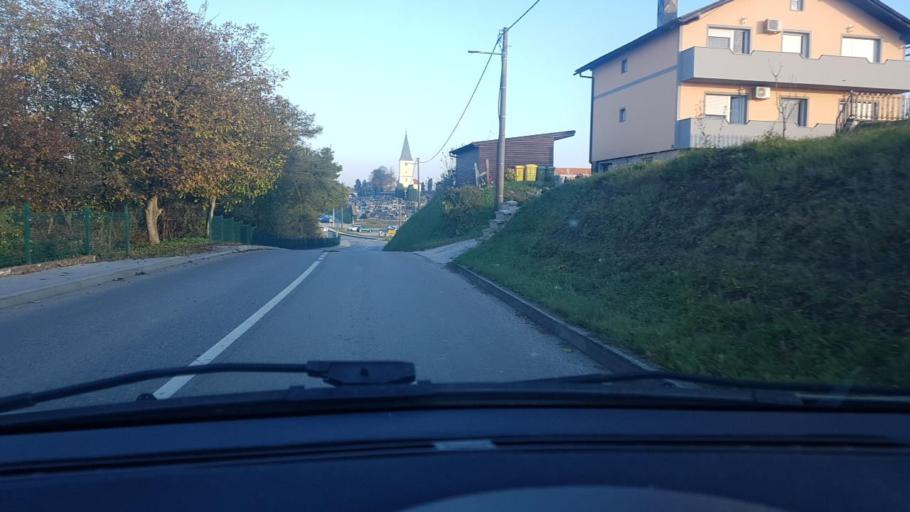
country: SI
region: Rogatec
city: Rogatec
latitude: 46.2124
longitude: 15.6800
